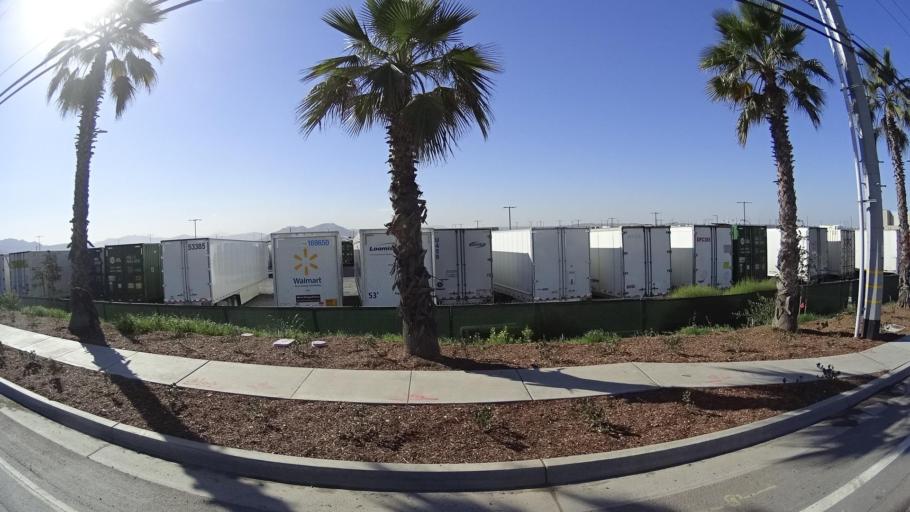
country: MX
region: Baja California
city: Tijuana
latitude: 32.5674
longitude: -116.9249
